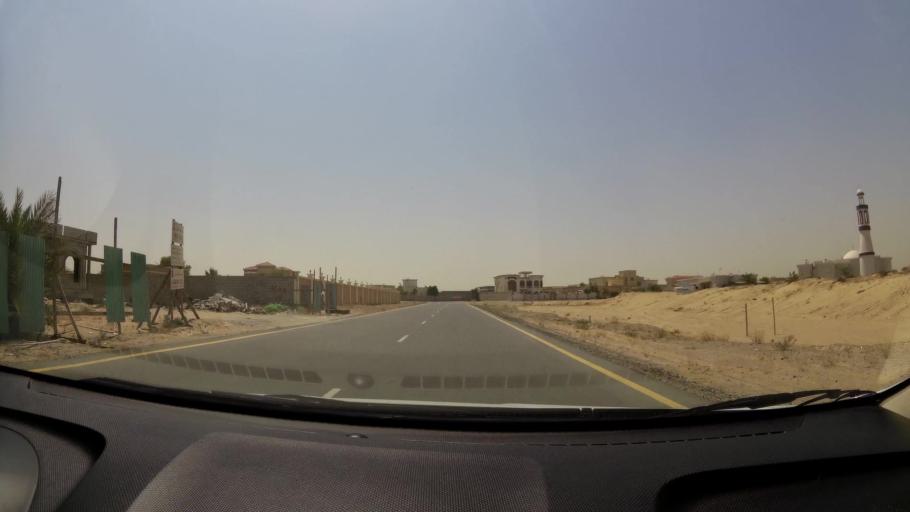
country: AE
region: Ajman
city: Ajman
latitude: 25.4183
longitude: 55.5255
